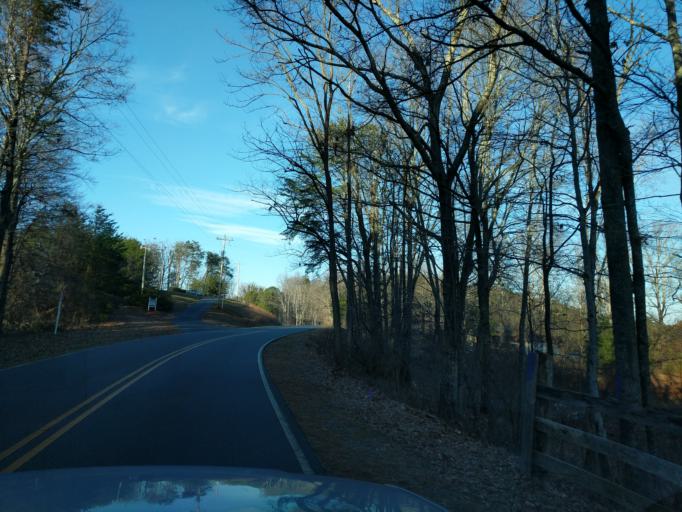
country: US
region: North Carolina
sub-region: Rutherford County
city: Lake Lure
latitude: 35.4074
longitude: -82.1723
